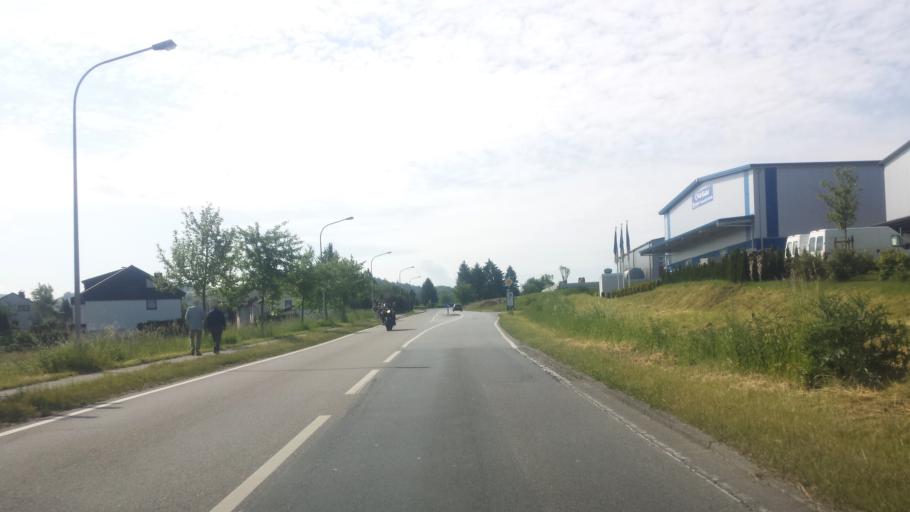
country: DE
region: Hesse
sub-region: Regierungsbezirk Darmstadt
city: Rimbach
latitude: 49.6083
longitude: 8.7569
